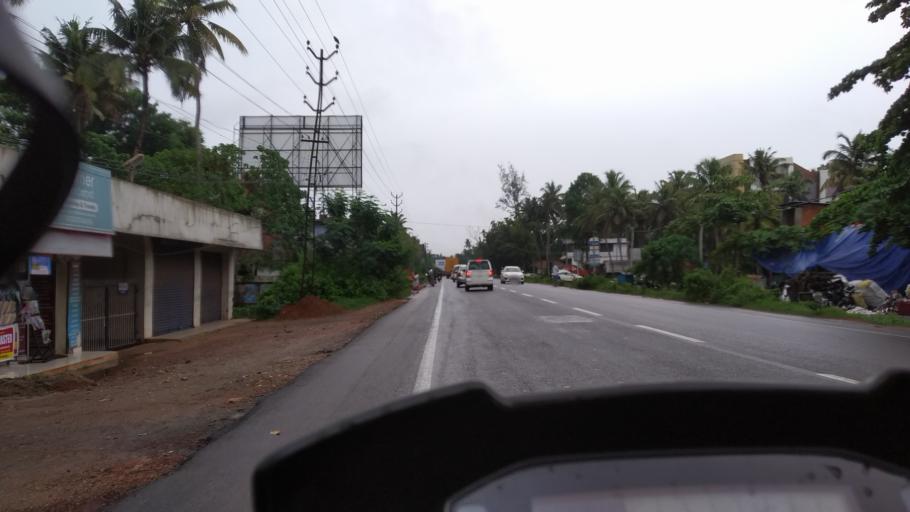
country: IN
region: Kerala
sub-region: Alappuzha
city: Kayankulam
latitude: 9.1223
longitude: 76.5177
